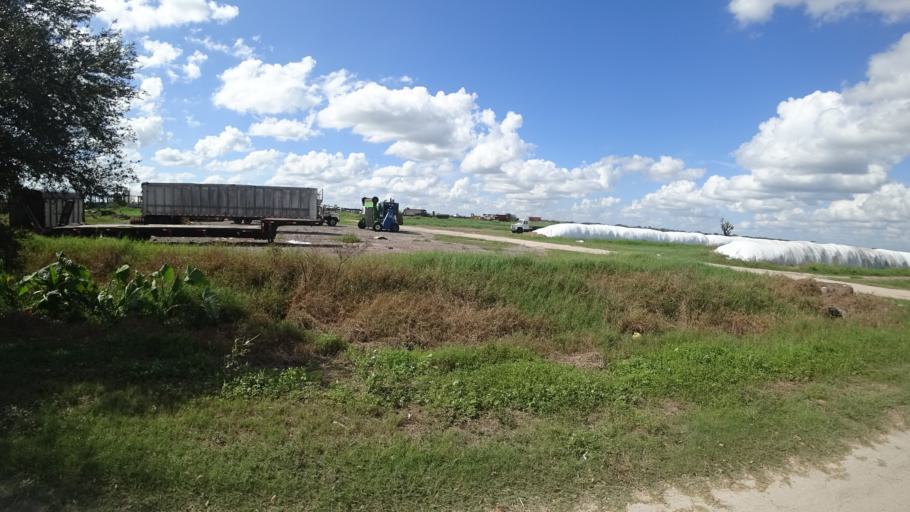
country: US
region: Florida
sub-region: Sarasota County
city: Warm Mineral Springs
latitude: 27.3166
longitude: -82.1305
